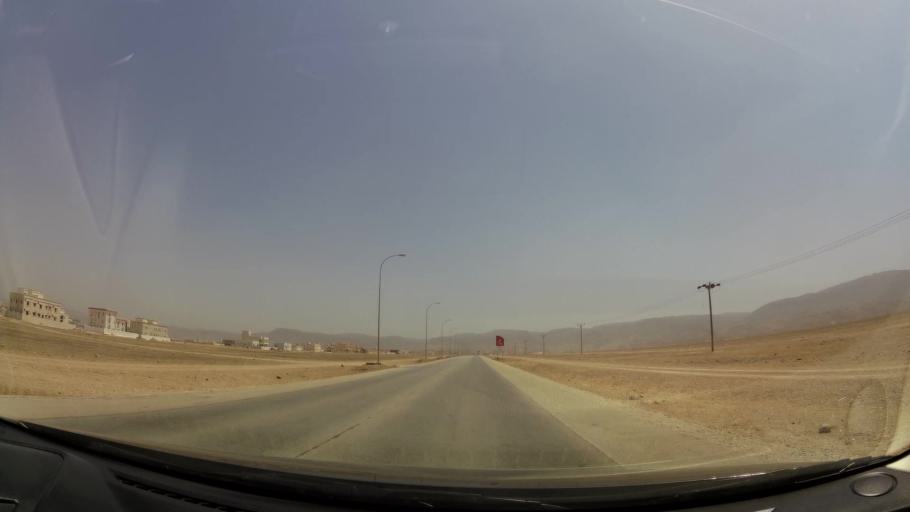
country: OM
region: Zufar
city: Salalah
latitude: 17.0879
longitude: 54.2170
